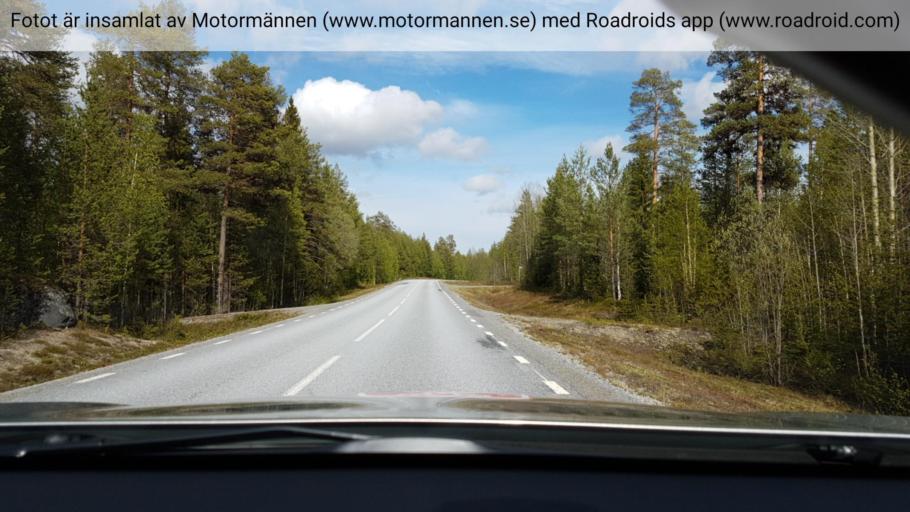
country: SE
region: Vaesterbotten
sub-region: Lycksele Kommun
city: Lycksele
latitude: 64.0612
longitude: 18.4806
